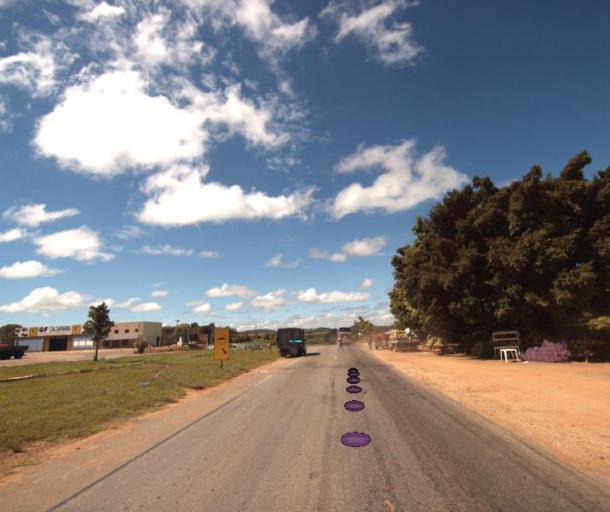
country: BR
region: Goias
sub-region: Rialma
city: Rialma
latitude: -15.4508
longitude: -49.5047
